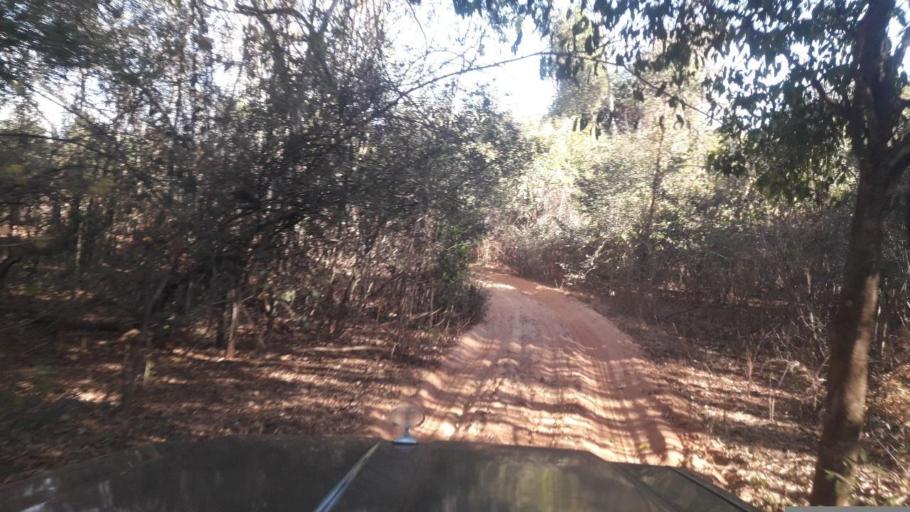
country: MG
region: Boeny
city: Sitampiky
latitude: -16.4203
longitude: 45.6184
